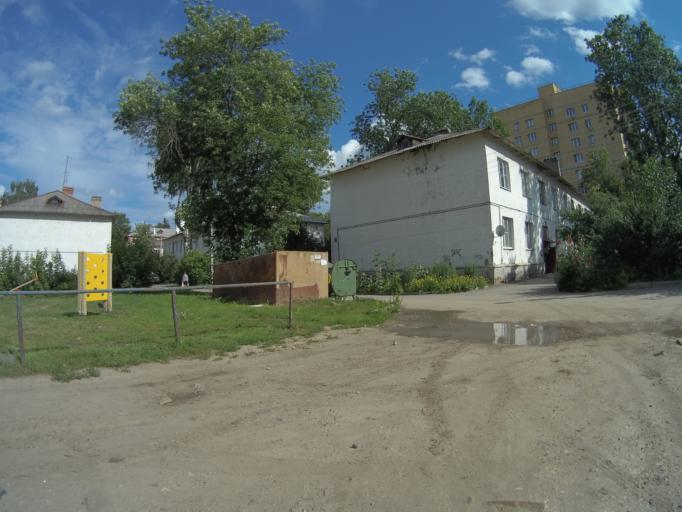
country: RU
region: Vladimir
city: Vladimir
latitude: 56.1411
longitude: 40.4240
